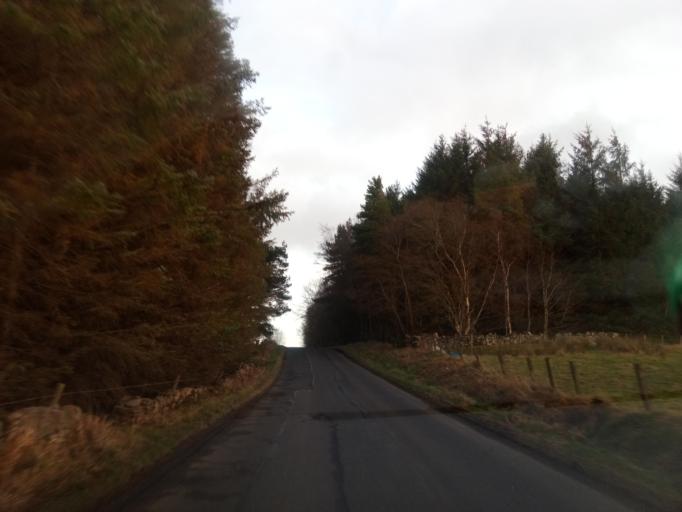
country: GB
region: Scotland
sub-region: The Scottish Borders
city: Selkirk
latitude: 55.5540
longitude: -2.7835
